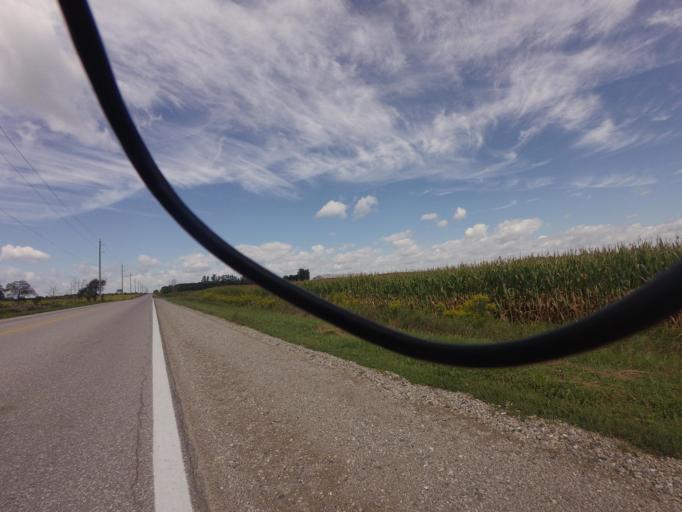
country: CA
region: Ontario
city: Stratford
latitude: 43.4961
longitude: -80.7953
